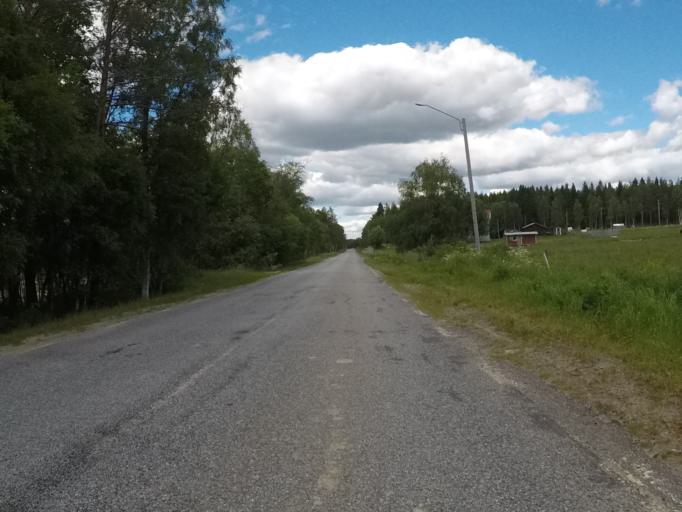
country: SE
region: Vaesterbotten
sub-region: Robertsfors Kommun
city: Robertsfors
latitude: 63.9918
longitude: 20.8102
